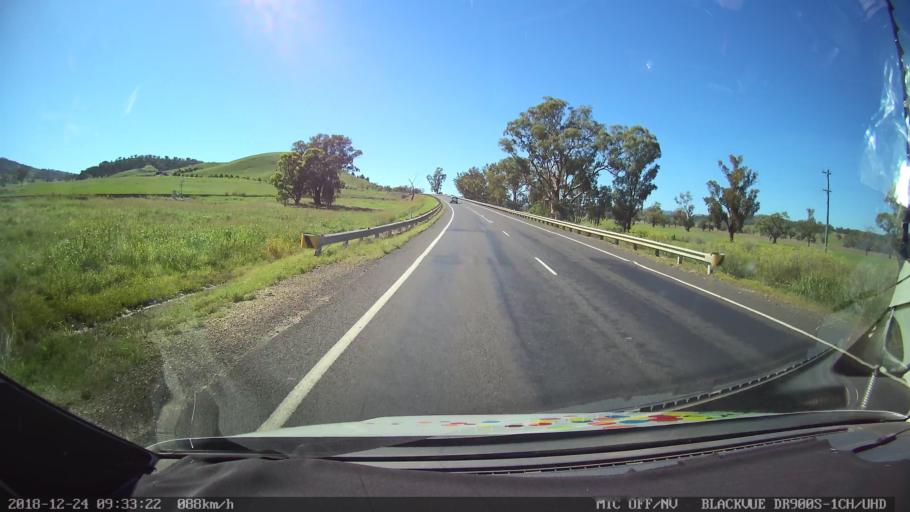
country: AU
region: New South Wales
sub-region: Liverpool Plains
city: Quirindi
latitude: -31.6027
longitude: 150.7068
